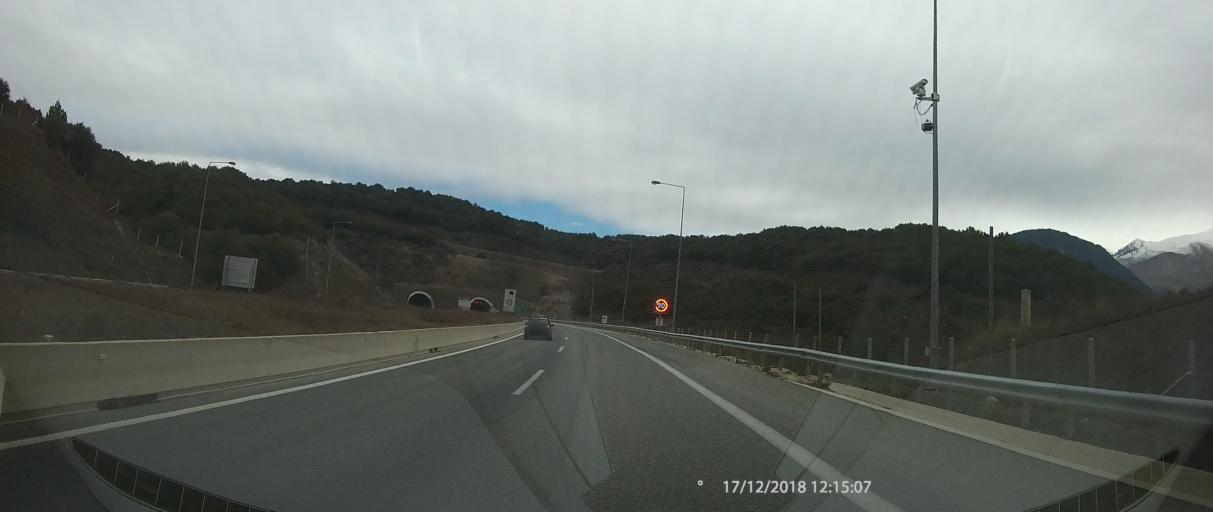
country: GR
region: Epirus
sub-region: Nomos Ioanninon
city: Katsikas
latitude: 39.7151
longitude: 21.0137
